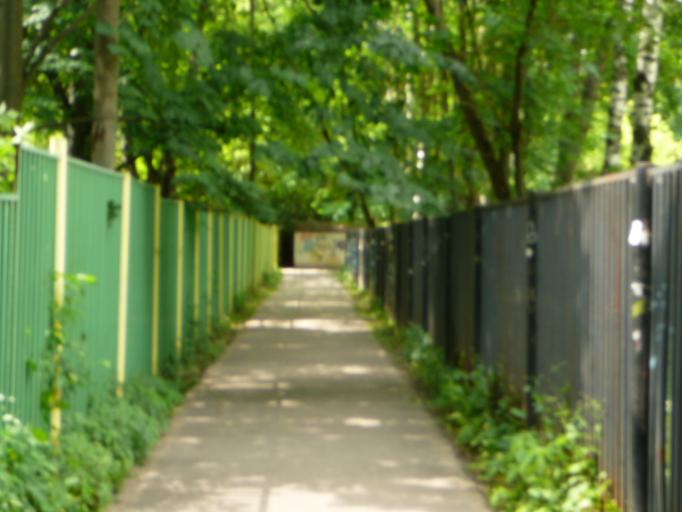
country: RU
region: Moskovskaya
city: Krasnogorsk
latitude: 55.8157
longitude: 37.3211
